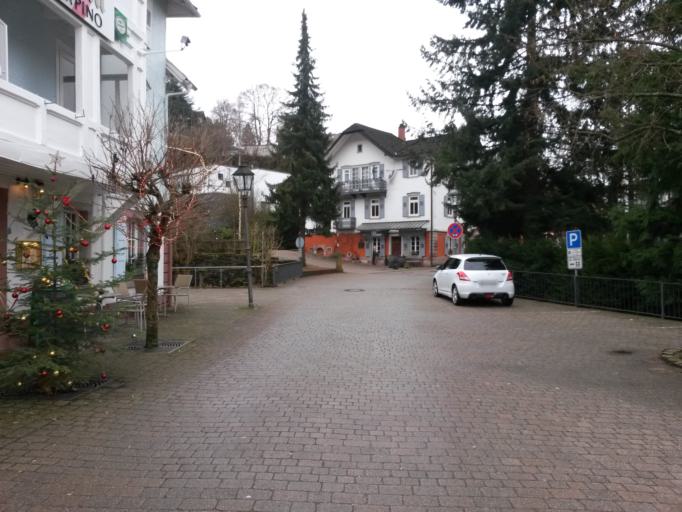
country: DE
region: Baden-Wuerttemberg
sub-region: Karlsruhe Region
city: Bad Herrenalb
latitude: 48.7954
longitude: 8.4382
